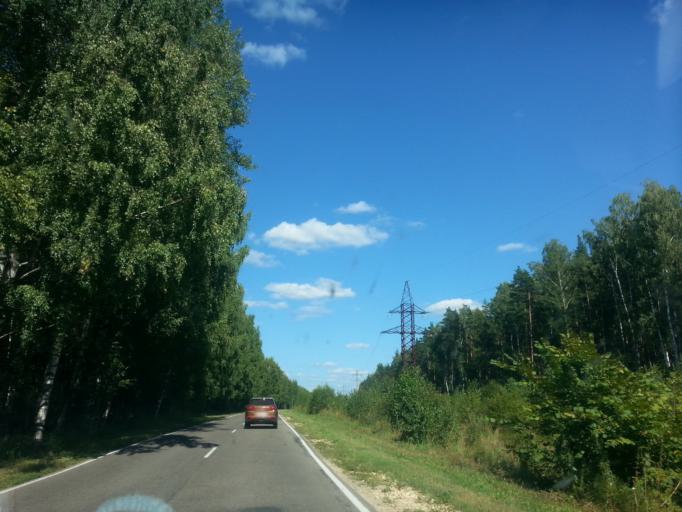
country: RU
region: Nizjnij Novgorod
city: Taremskoye
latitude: 56.0068
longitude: 42.9190
